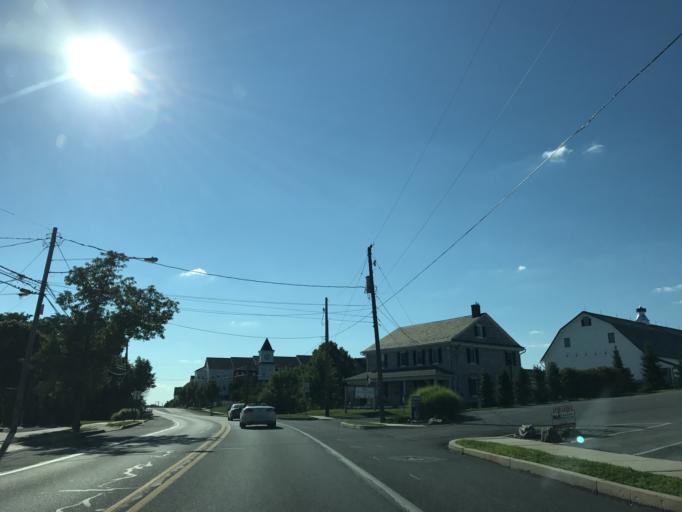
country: US
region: Pennsylvania
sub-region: Lancaster County
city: Mount Joy
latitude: 40.1157
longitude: -76.5256
